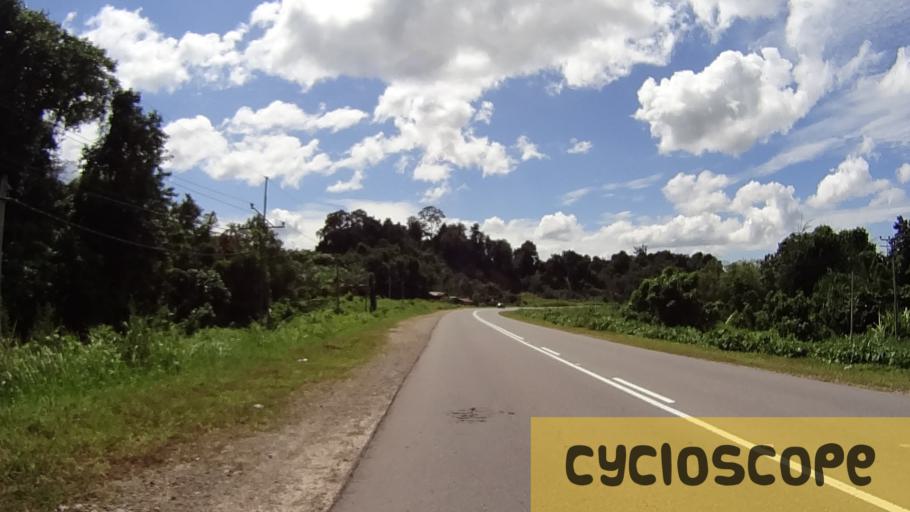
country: MY
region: Sabah
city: Beaufort
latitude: 5.2215
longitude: 115.6441
